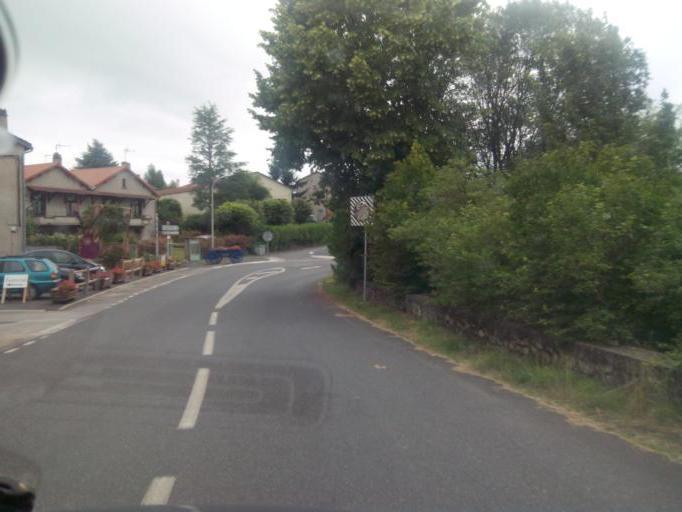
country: FR
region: Rhone-Alpes
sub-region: Departement de la Loire
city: Usson-en-Forez
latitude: 45.3558
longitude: 3.9550
